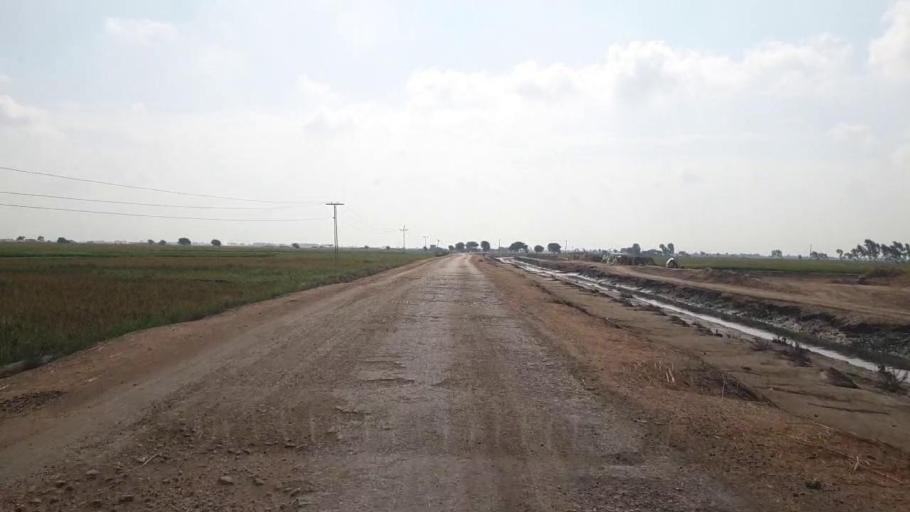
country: PK
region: Sindh
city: Kario
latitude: 24.6213
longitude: 68.5562
